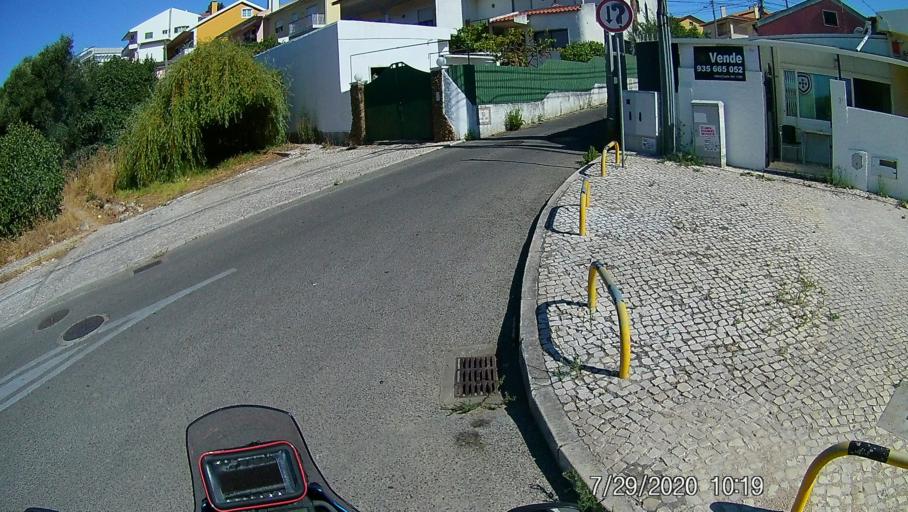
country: PT
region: Lisbon
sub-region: Cascais
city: Estoril
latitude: 38.7238
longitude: -9.3756
